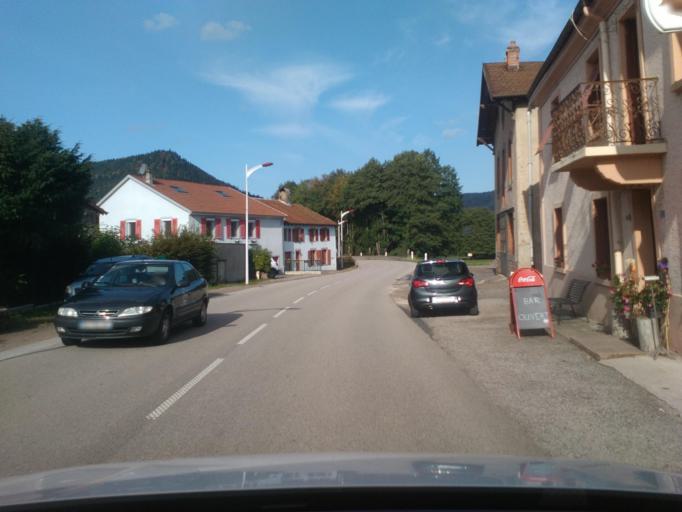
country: FR
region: Lorraine
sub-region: Departement des Vosges
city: Senones
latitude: 48.4094
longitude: 7.0509
